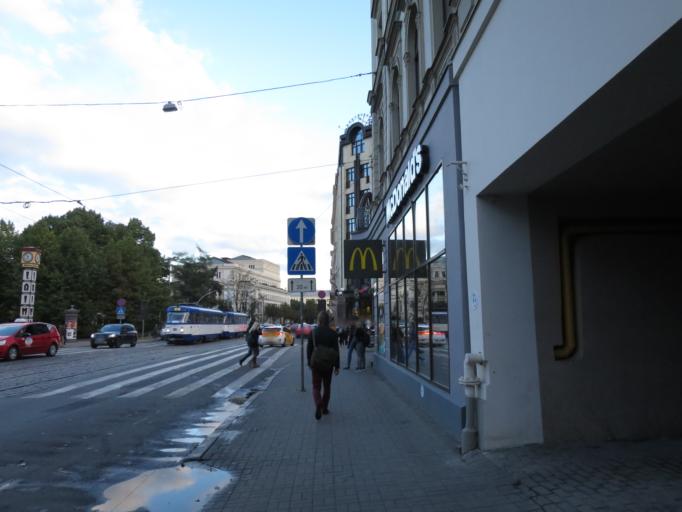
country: LV
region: Riga
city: Riga
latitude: 56.9506
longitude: 24.1113
